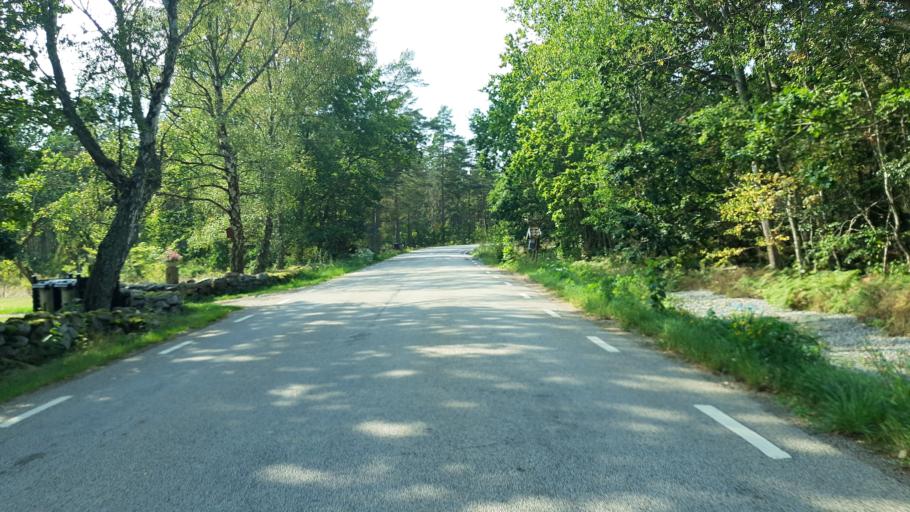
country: SE
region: Blekinge
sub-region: Ronneby Kommun
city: Ronneby
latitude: 56.1653
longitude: 15.1951
